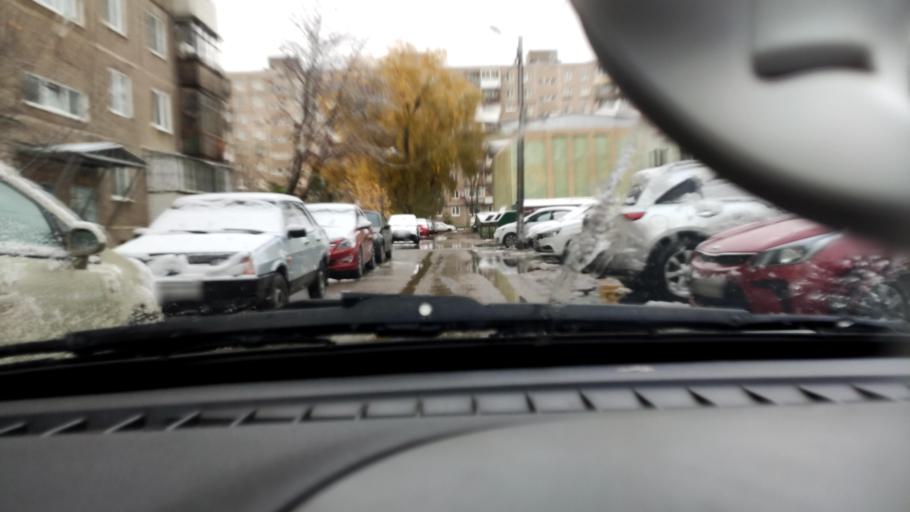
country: RU
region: Perm
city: Kondratovo
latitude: 57.9651
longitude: 56.1805
